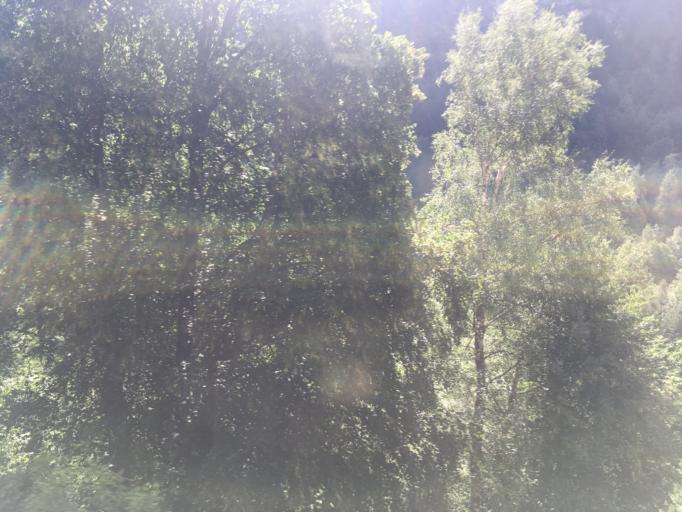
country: CH
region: Valais
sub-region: Visp District
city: Grachen
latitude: 46.2172
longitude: 7.8402
